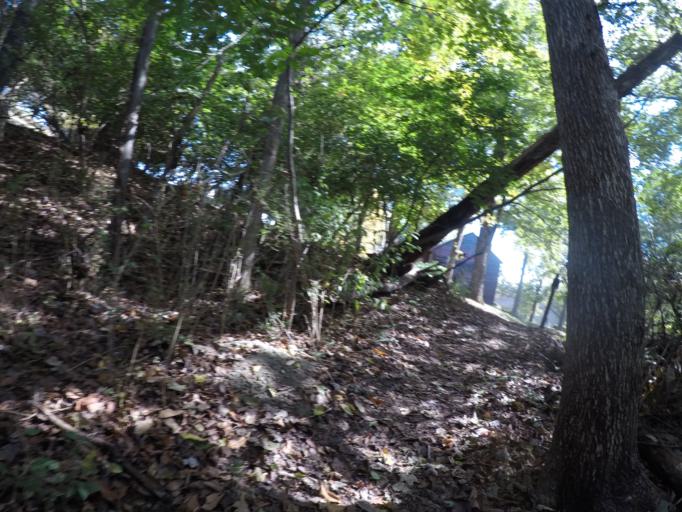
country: US
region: West Virginia
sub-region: Cabell County
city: Huntington
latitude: 38.3923
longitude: -82.3949
